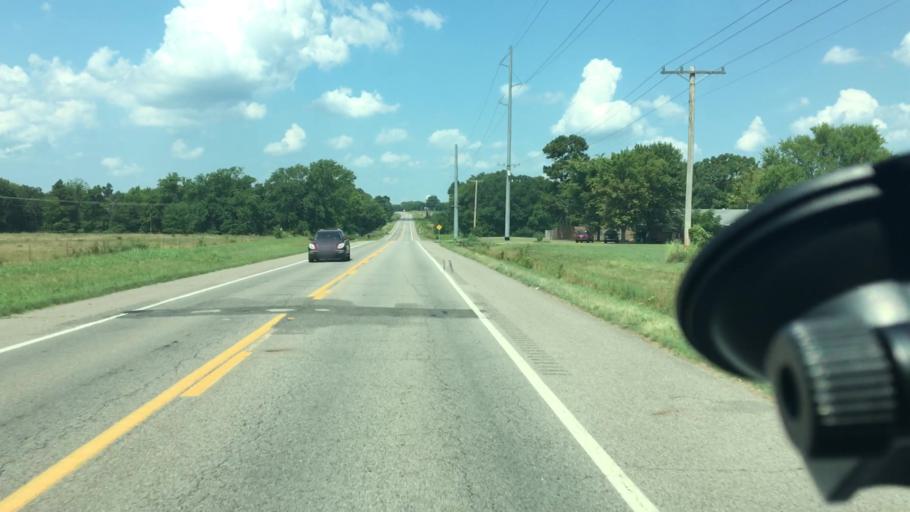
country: US
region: Arkansas
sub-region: Logan County
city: Paris
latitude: 35.2950
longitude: -93.6748
